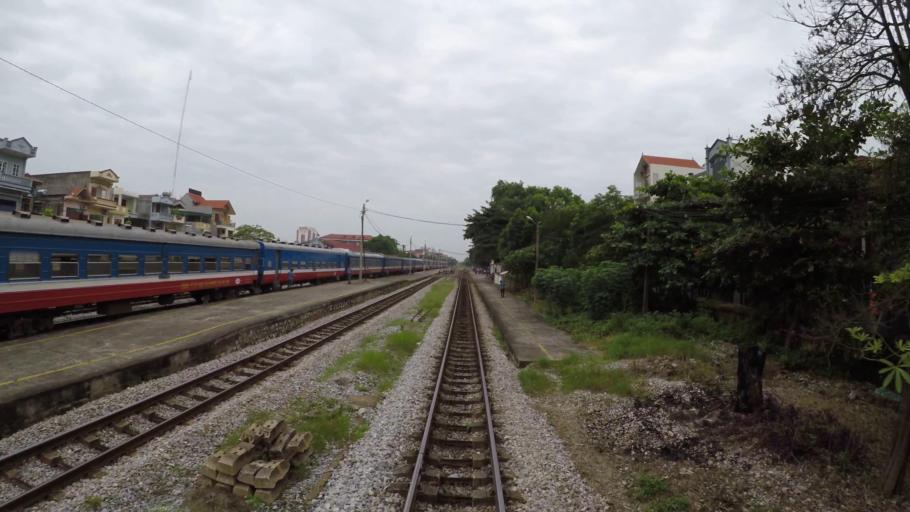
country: VN
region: Hai Duong
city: Thanh Pho Hai Duong
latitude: 20.9428
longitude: 106.2967
